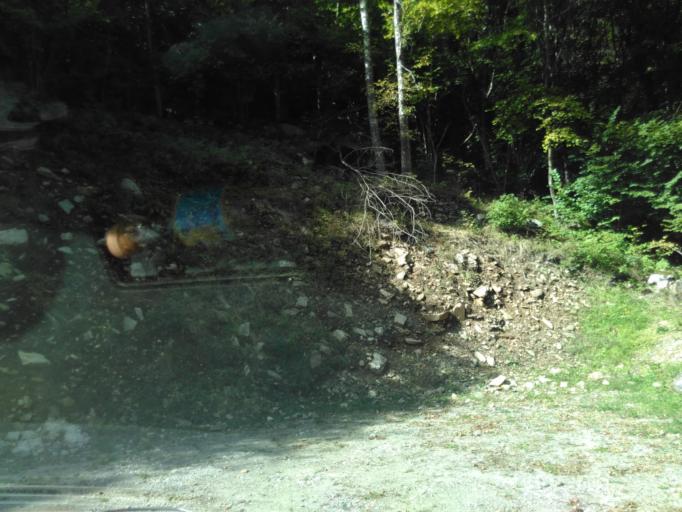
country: CH
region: Grisons
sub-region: Moesa District
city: Cauco
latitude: 46.3723
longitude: 9.1232
